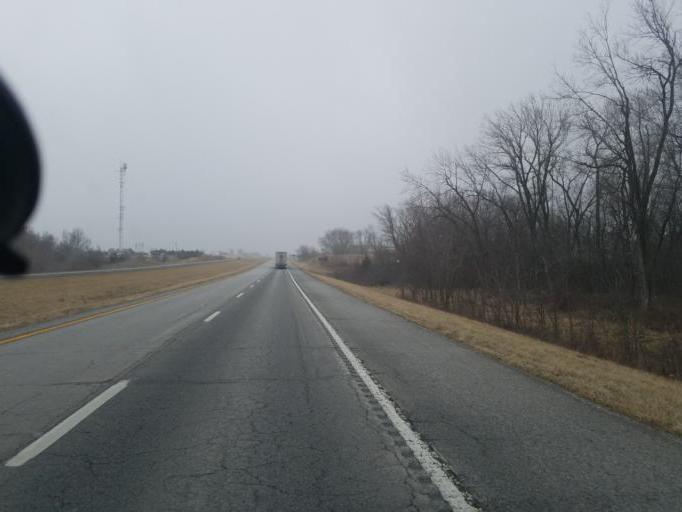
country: US
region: Missouri
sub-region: Macon County
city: La Plata
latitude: 39.9233
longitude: -92.4753
